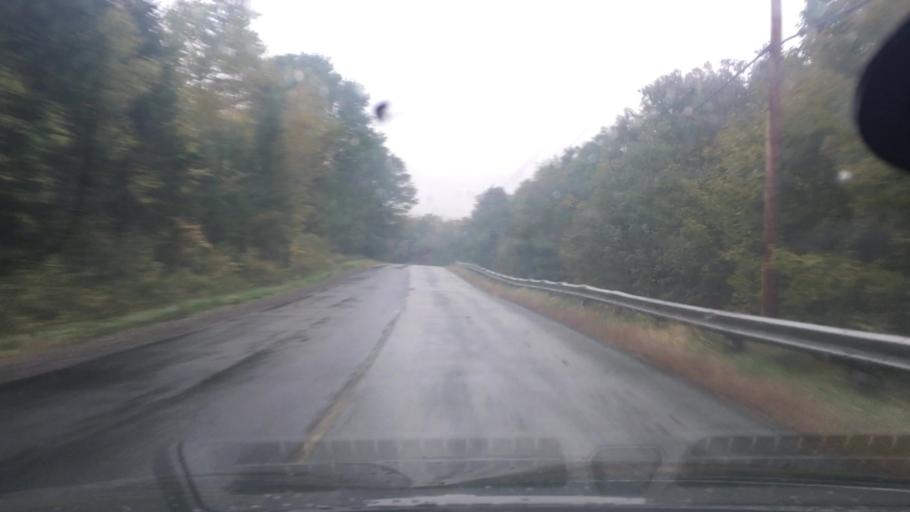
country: CA
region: Nova Scotia
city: Windsor
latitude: 44.8335
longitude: -64.2587
